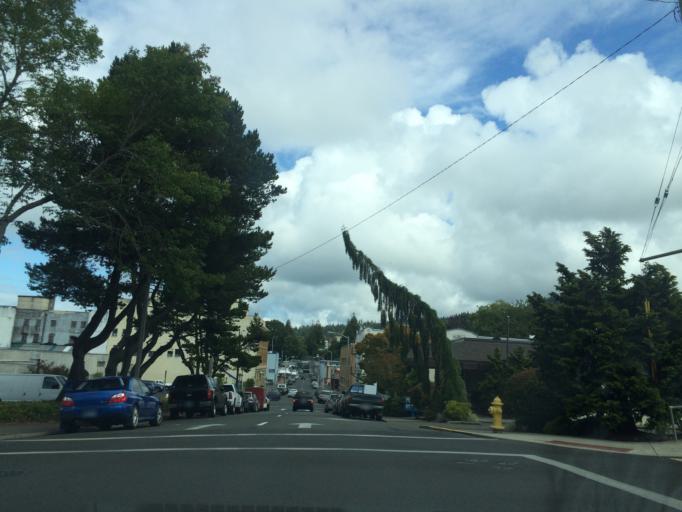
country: US
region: Oregon
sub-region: Clatsop County
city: Astoria
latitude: 46.1877
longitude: -123.8340
